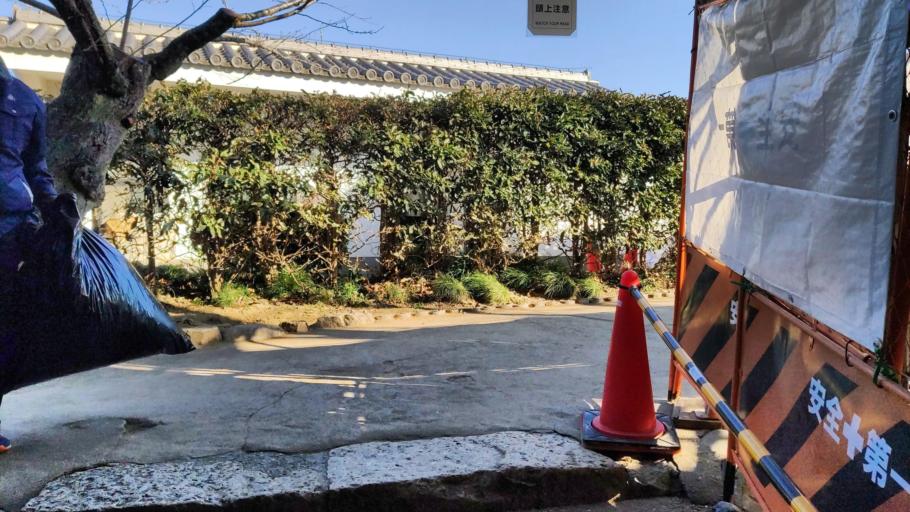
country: JP
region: Hyogo
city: Himeji
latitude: 34.8397
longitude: 134.6933
